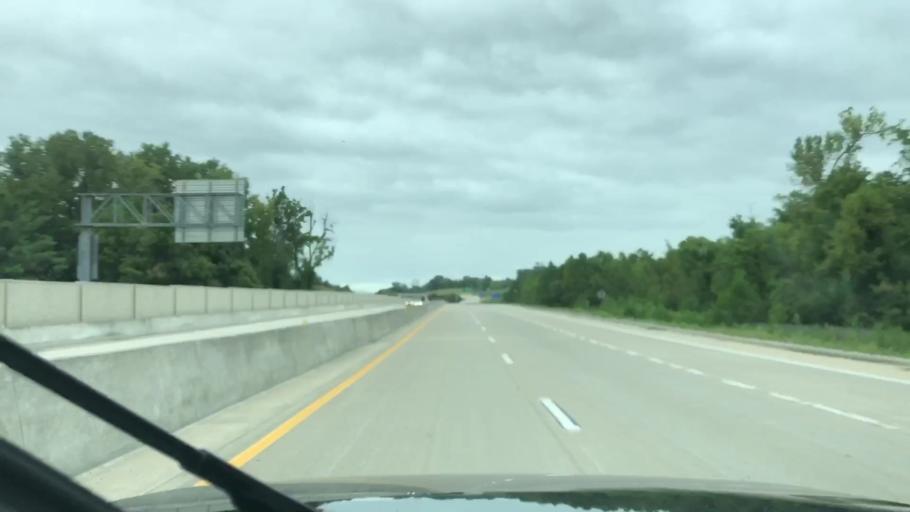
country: US
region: Missouri
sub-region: Saint Louis County
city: Town and Country
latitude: 38.6741
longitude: -90.4937
